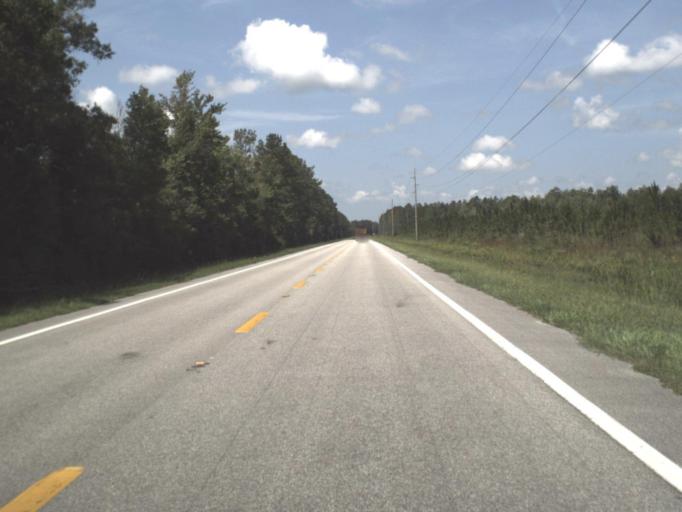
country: US
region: Florida
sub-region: Levy County
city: Bronson
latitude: 29.3479
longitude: -82.7408
